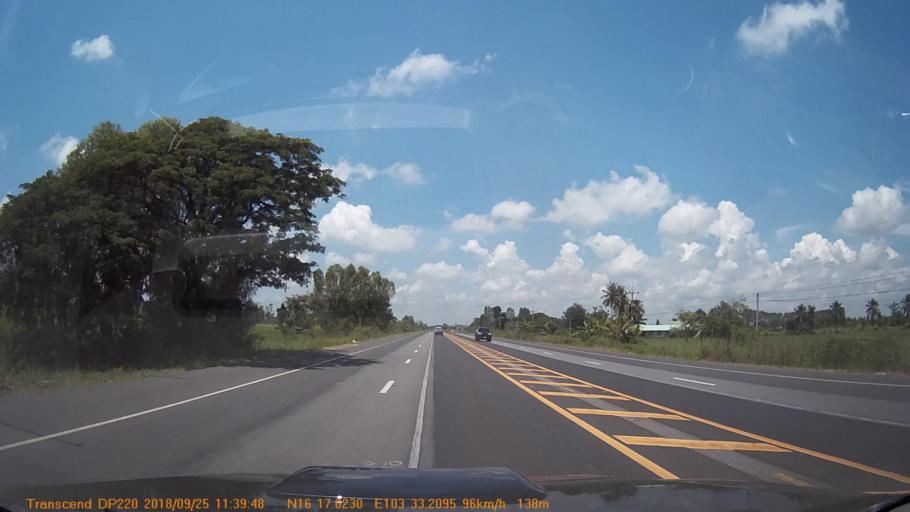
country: TH
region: Kalasin
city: Kamalasai
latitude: 16.2837
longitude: 103.5535
